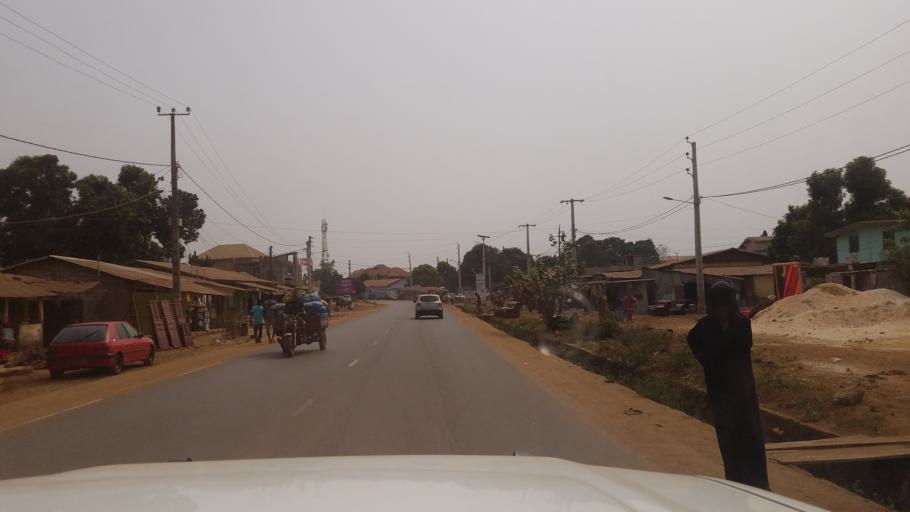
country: GN
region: Kindia
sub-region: Prefecture de Dubreka
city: Dubreka
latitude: 9.6690
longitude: -13.5875
